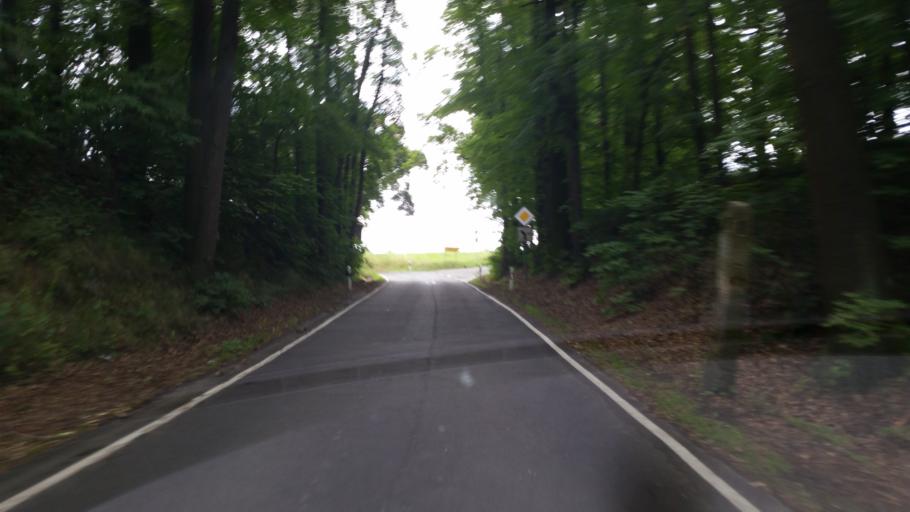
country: DE
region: Saxony
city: Crostwitz
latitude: 51.2293
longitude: 14.2613
